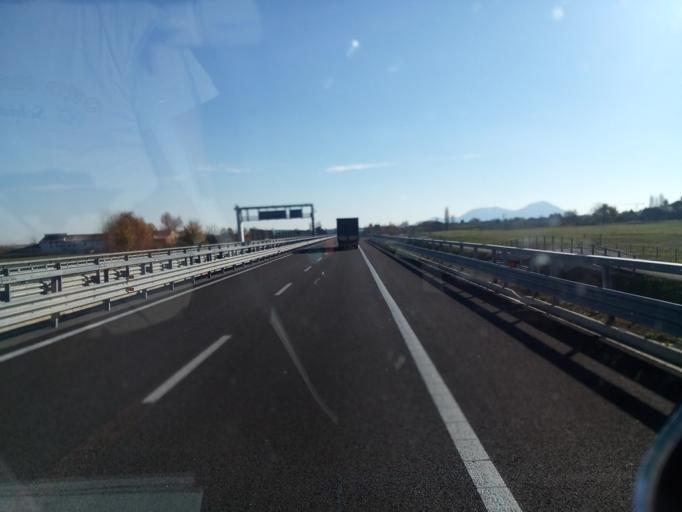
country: IT
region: Veneto
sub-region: Provincia di Vicenza
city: Longare
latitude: 45.4931
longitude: 11.6191
